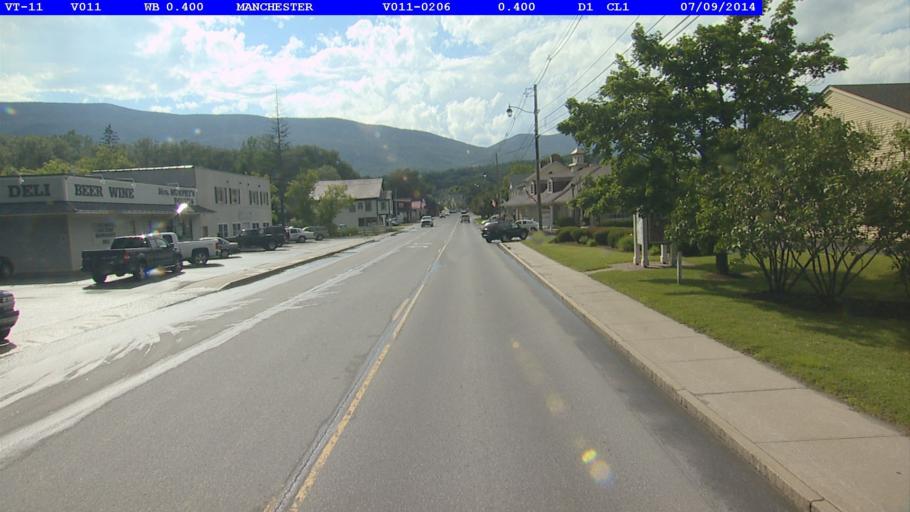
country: US
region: Vermont
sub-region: Bennington County
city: Manchester Center
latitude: 43.1738
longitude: -73.0502
